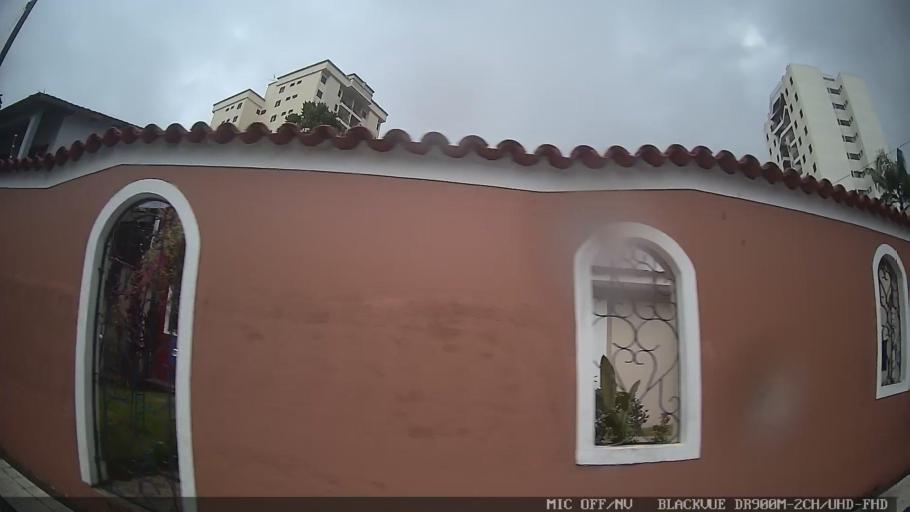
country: BR
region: Sao Paulo
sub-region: Mogi das Cruzes
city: Mogi das Cruzes
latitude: -23.5207
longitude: -46.1765
